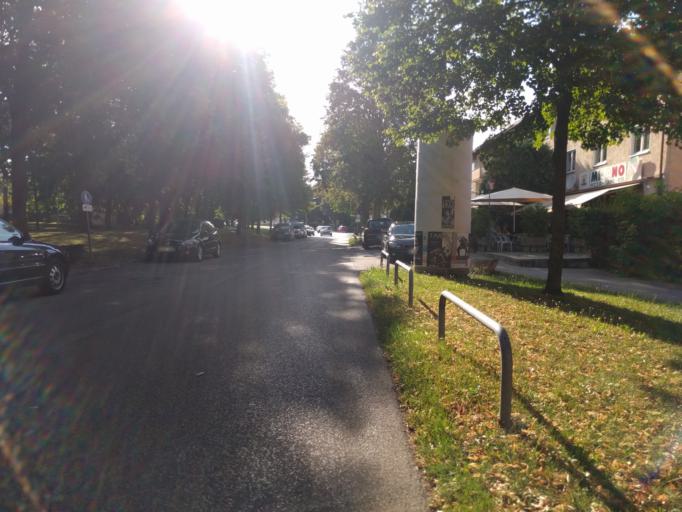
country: DE
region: Bavaria
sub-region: Upper Palatinate
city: Regensburg
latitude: 49.0019
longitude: 12.1163
